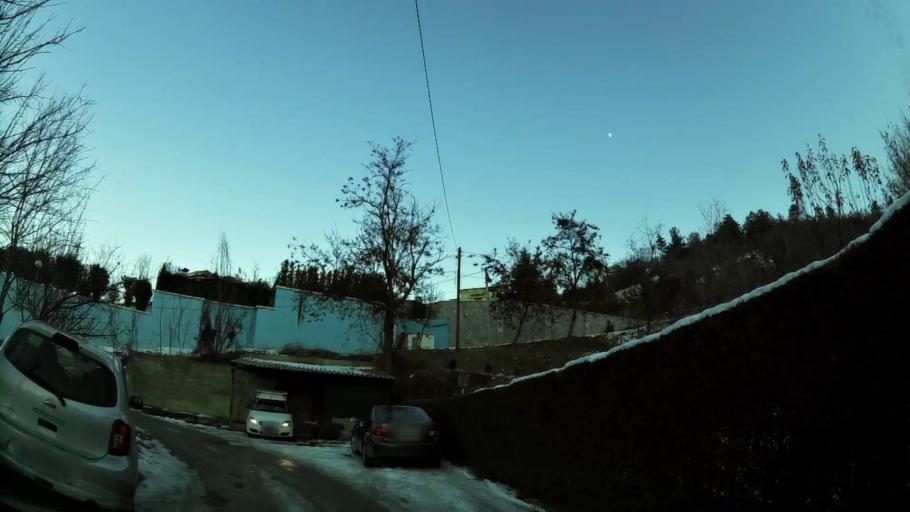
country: MK
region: Karpos
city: Skopje
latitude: 41.9898
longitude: 21.4078
